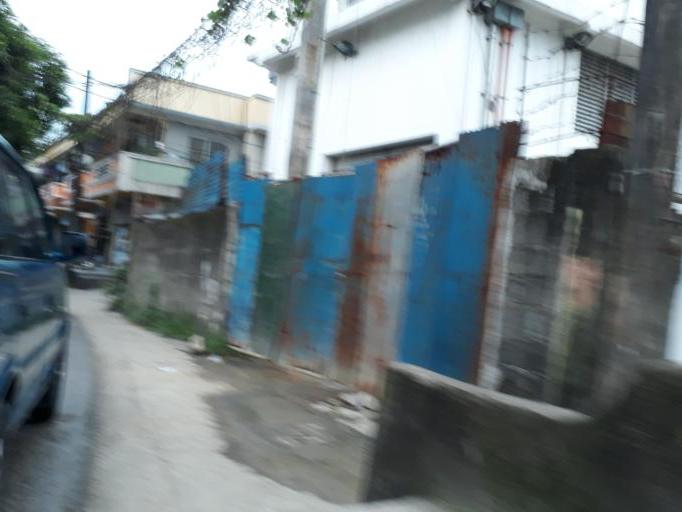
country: PH
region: Calabarzon
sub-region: Province of Rizal
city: Valenzuela
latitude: 14.6959
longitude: 120.9955
